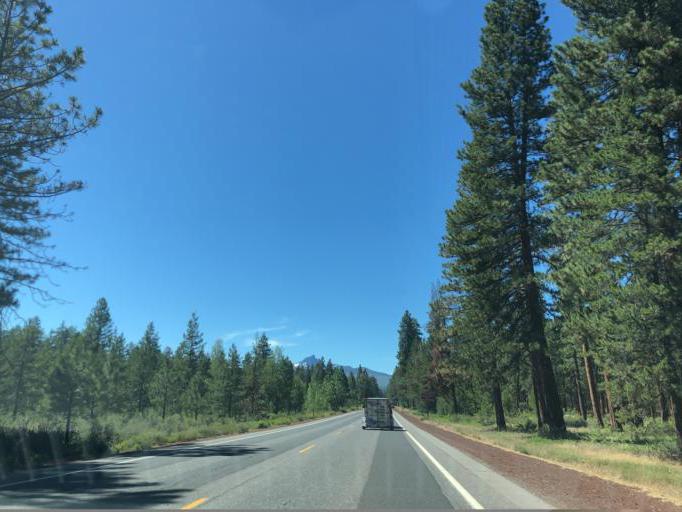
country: US
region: Oregon
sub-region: Deschutes County
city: Sisters
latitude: 44.3847
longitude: -121.6620
